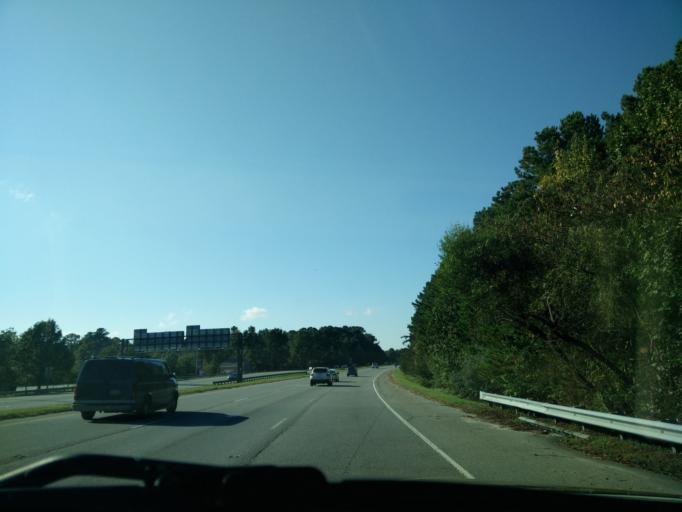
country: US
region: Virginia
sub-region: City of Chesapeake
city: Chesapeake
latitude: 36.7380
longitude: -76.2452
